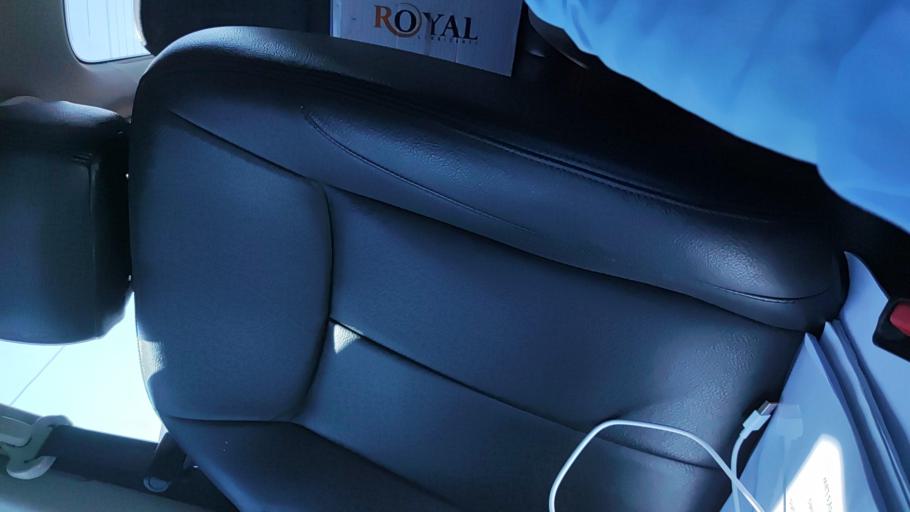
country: IQ
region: Arbil
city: Erbil
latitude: 36.1863
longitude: 44.0211
